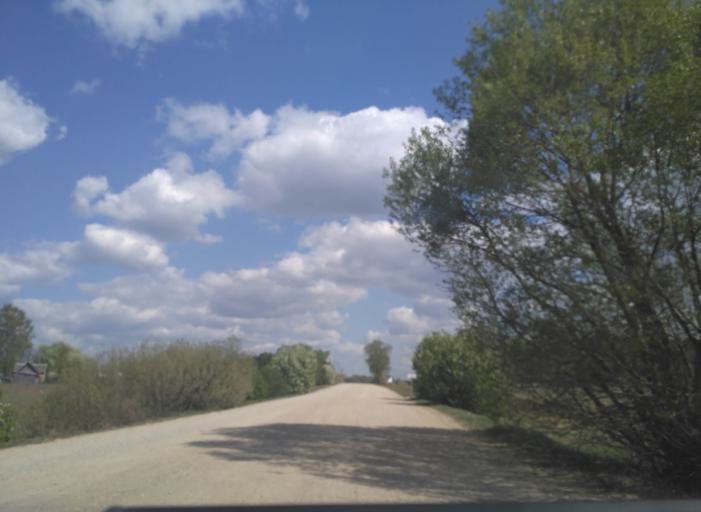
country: BY
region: Minsk
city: Radashkovichy
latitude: 54.2104
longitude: 27.2805
